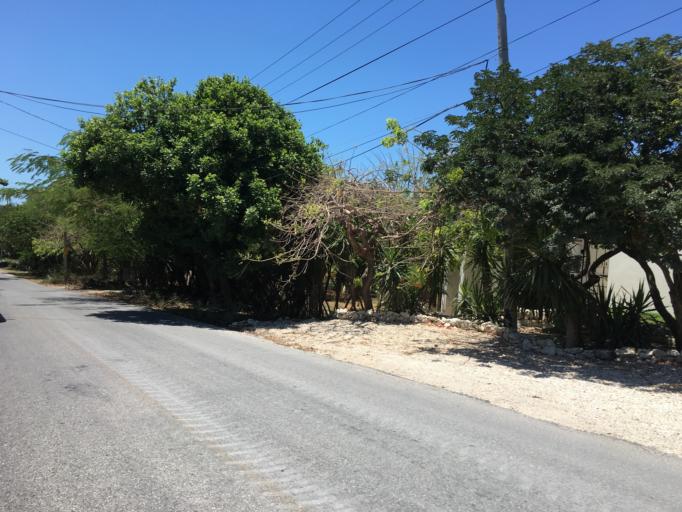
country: MX
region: Quintana Roo
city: Isla Mujeres
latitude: 21.2095
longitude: -86.7196
